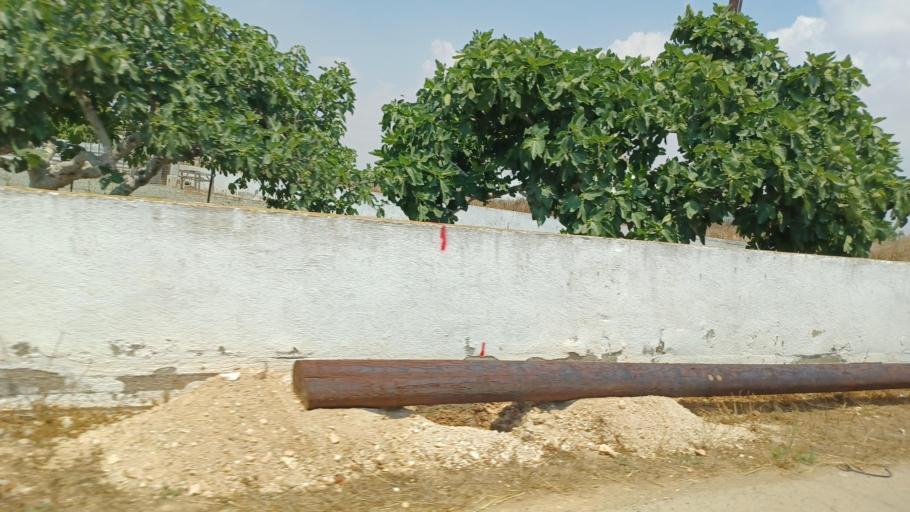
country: CY
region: Ammochostos
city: Liopetri
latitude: 34.9849
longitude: 33.8500
